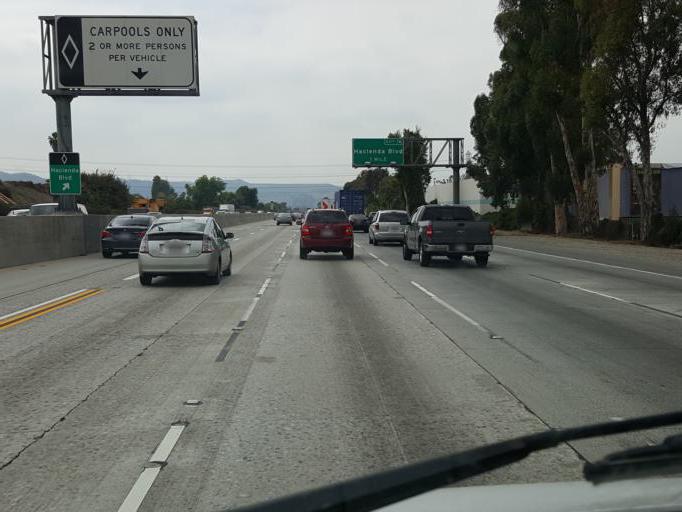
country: US
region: California
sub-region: Los Angeles County
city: La Puente
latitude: 34.0006
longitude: -117.9433
